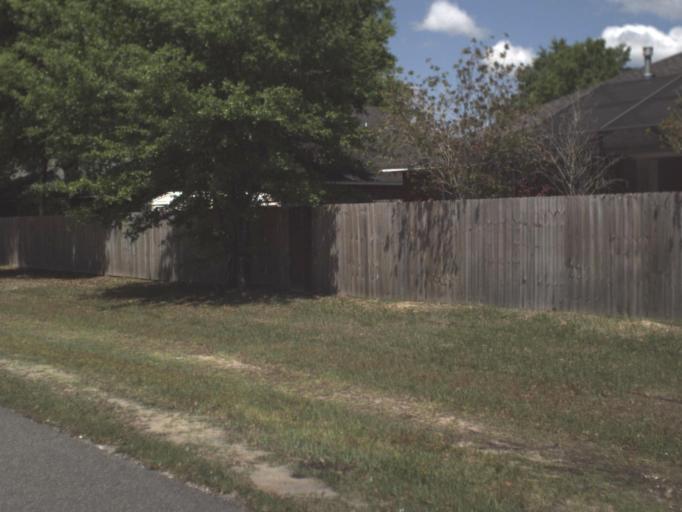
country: US
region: Florida
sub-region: Escambia County
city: Myrtle Grove
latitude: 30.4004
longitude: -87.3847
